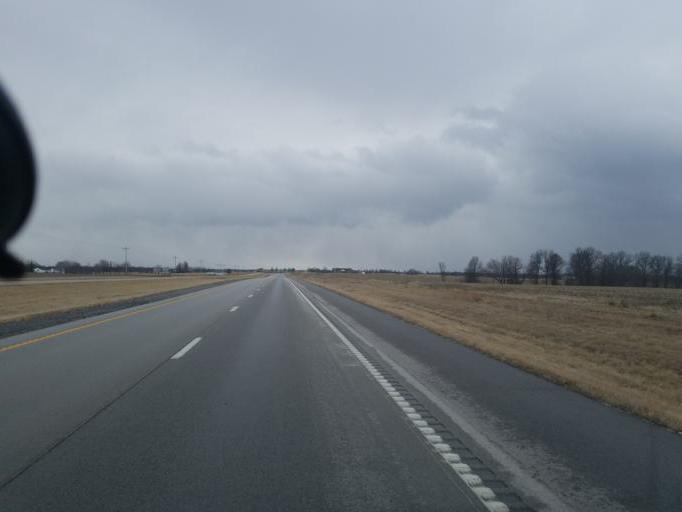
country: US
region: Missouri
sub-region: Macon County
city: Macon
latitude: 39.8085
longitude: -92.4746
